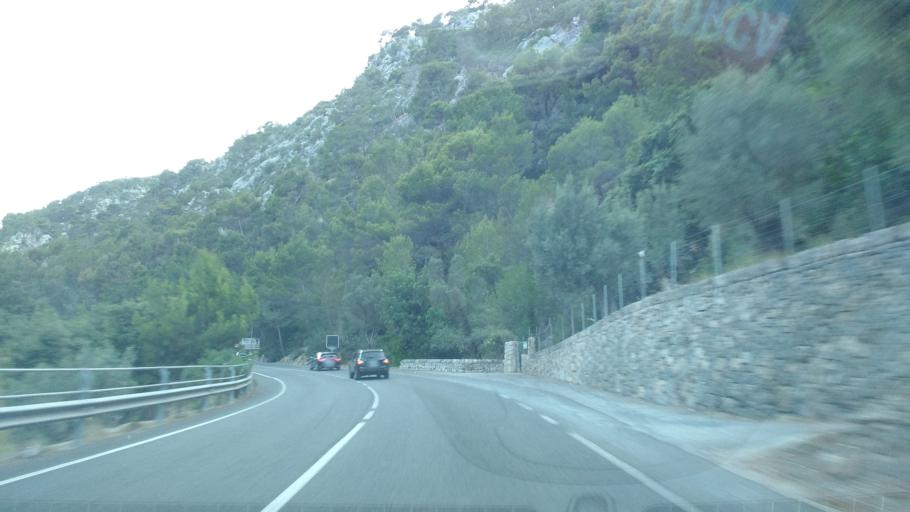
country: ES
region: Balearic Islands
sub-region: Illes Balears
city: Soller
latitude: 39.7476
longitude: 2.6993
